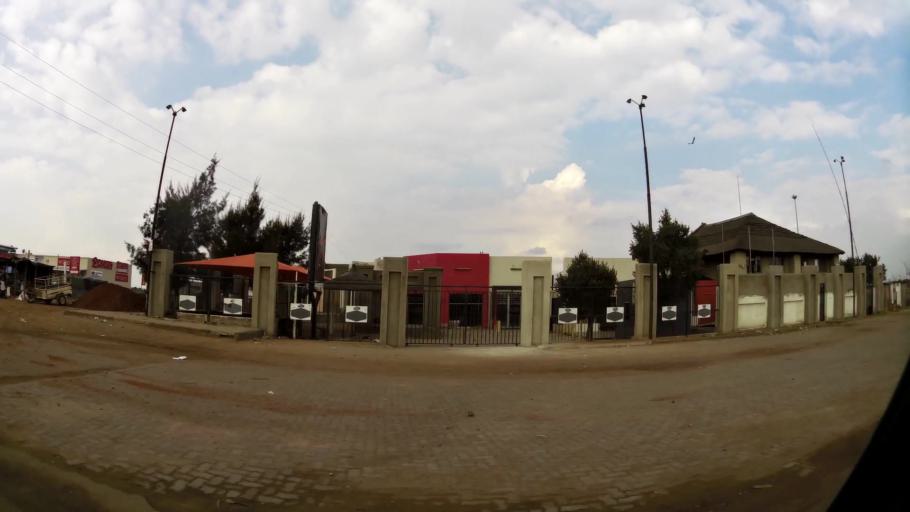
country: ZA
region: Gauteng
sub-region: Sedibeng District Municipality
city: Vanderbijlpark
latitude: -26.6667
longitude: 27.8636
